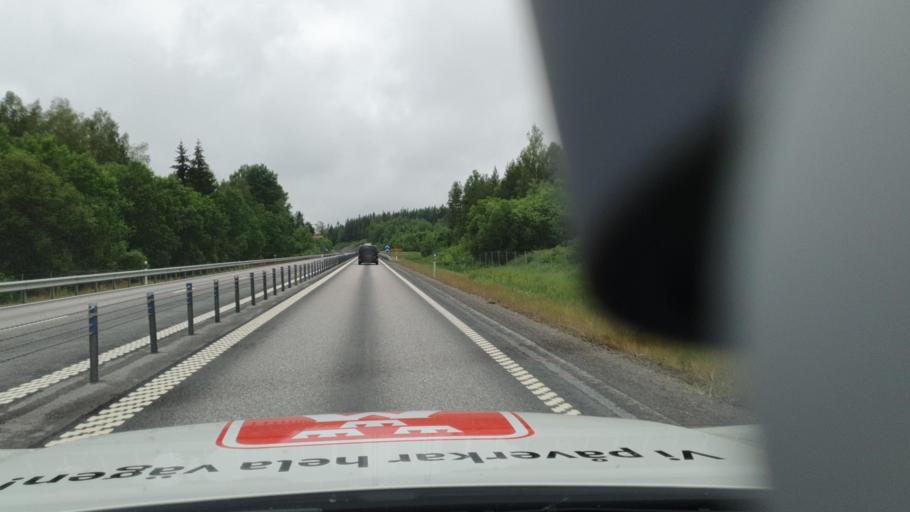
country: SE
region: OErebro
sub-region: Degerfors Kommun
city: Degerfors
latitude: 59.3226
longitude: 14.3891
